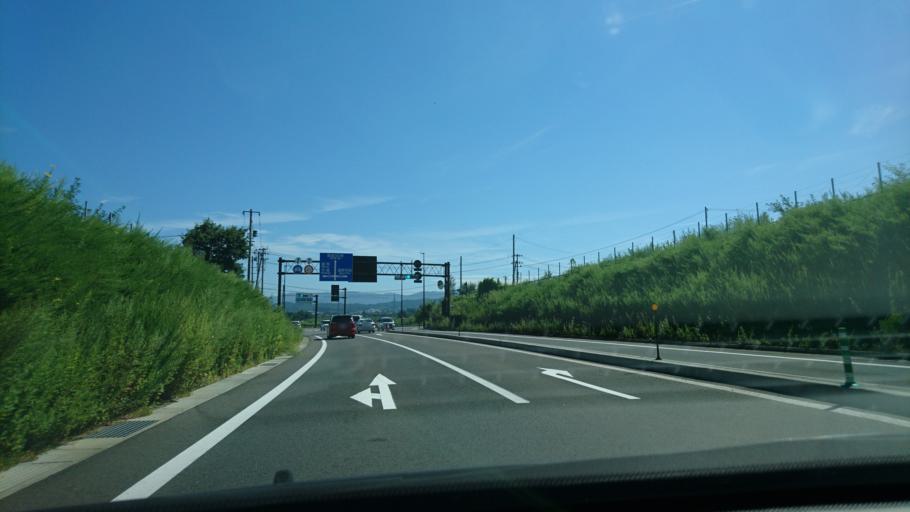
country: JP
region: Iwate
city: Tono
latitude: 39.3264
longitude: 141.5069
